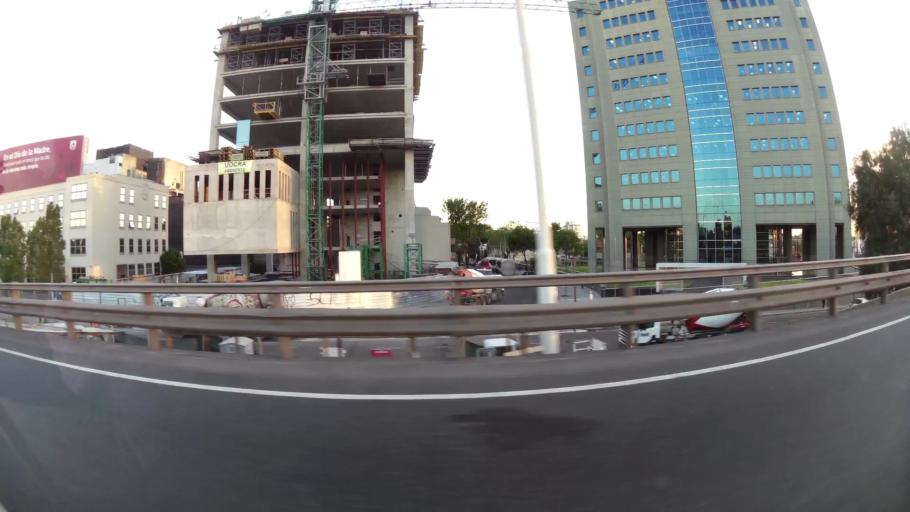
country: AR
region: Buenos Aires
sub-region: Partido de Vicente Lopez
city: Olivos
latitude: -34.5465
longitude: -58.4911
